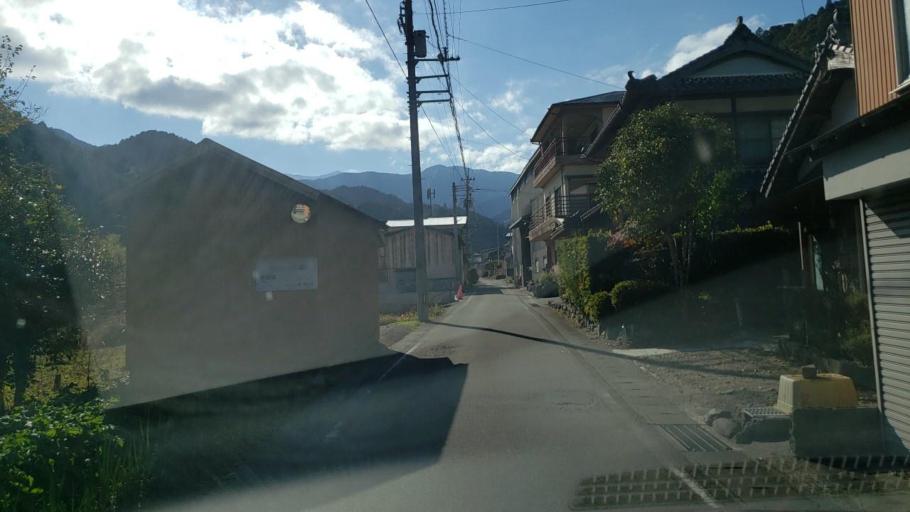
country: JP
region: Tokushima
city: Wakimachi
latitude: 33.9991
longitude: 134.0292
